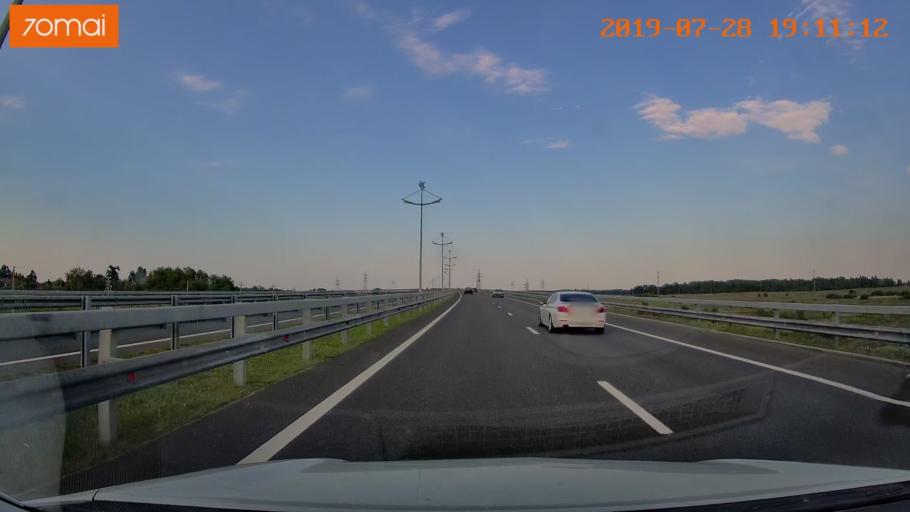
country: RU
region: Kaliningrad
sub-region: Gorod Kaliningrad
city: Pionerskiy
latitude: 54.9117
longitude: 20.2240
